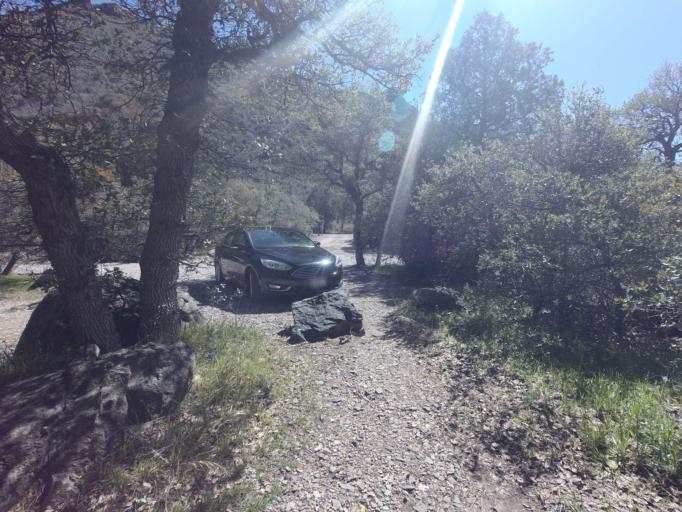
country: US
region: Arizona
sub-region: Coconino County
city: Sedona
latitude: 34.9560
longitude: -111.7552
